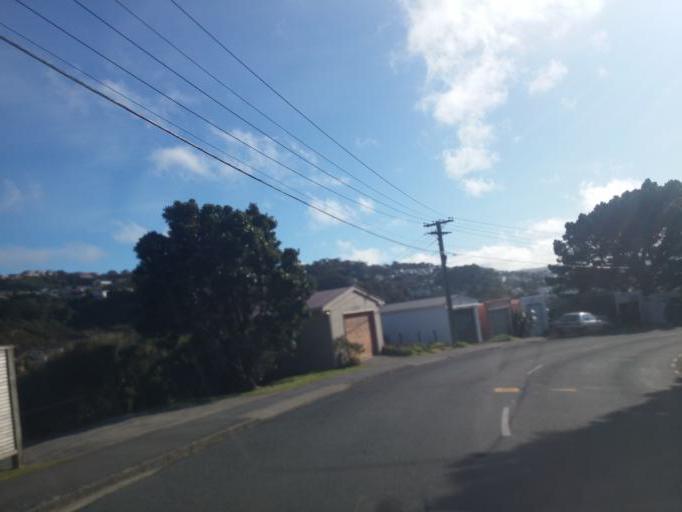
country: NZ
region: Wellington
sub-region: Wellington City
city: Brooklyn
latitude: -41.3122
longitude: 174.7637
